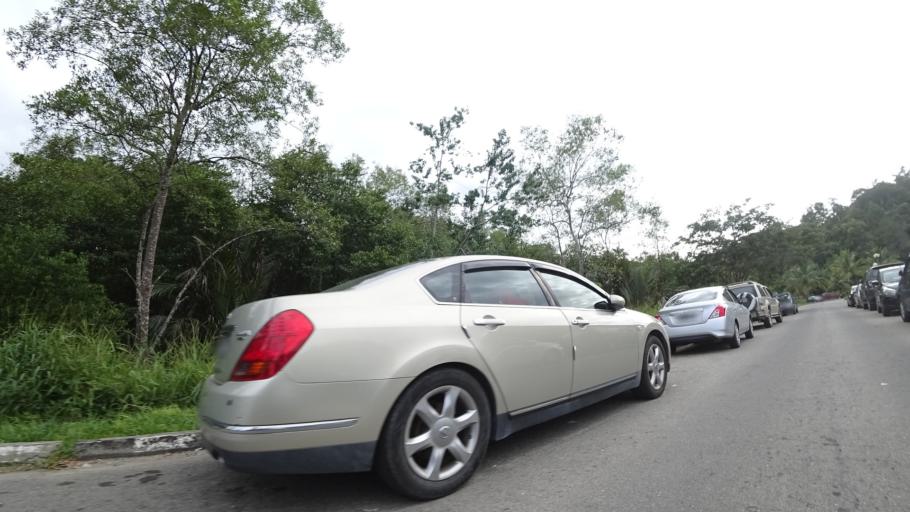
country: BN
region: Brunei and Muara
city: Bandar Seri Begawan
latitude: 4.8522
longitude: 114.9555
